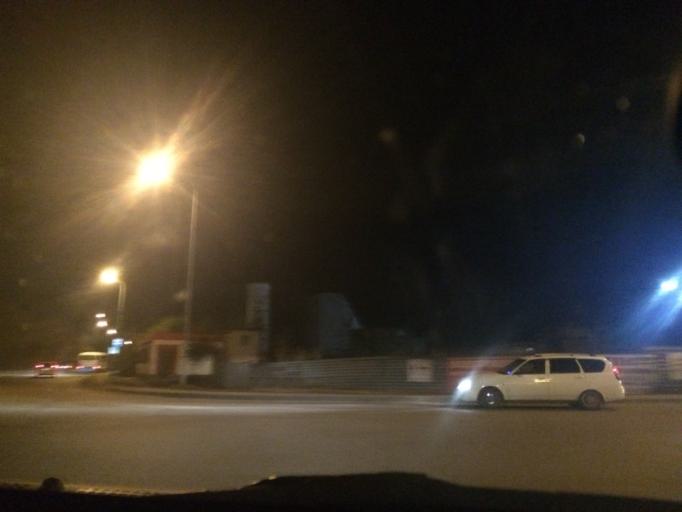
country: KZ
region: Astana Qalasy
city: Astana
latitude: 51.2051
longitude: 71.3785
